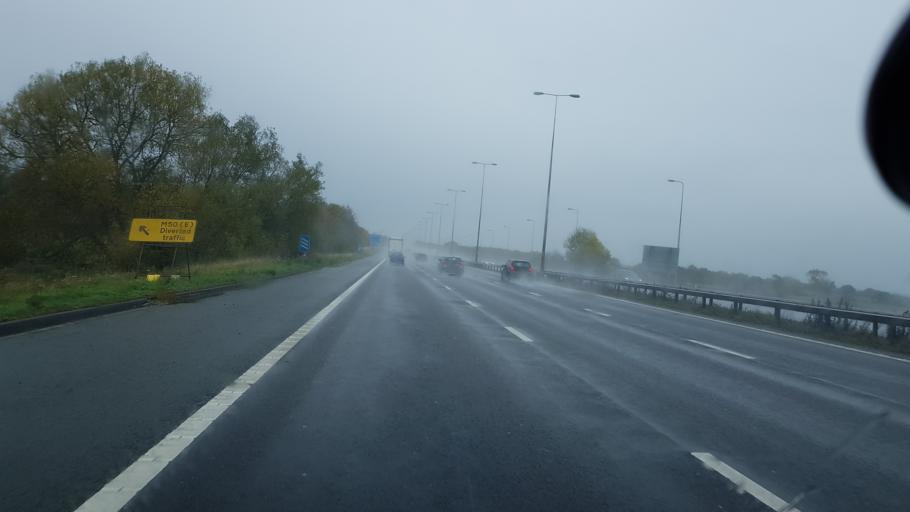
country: GB
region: England
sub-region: Worcestershire
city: Bredon
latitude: 52.0392
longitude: -2.1306
